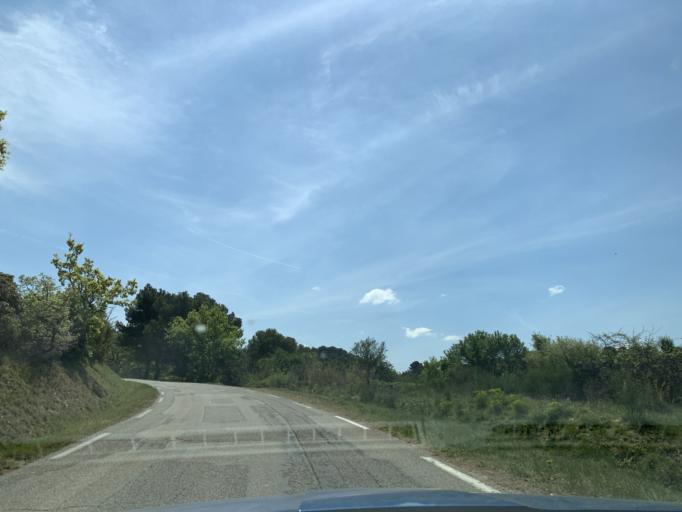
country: FR
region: Provence-Alpes-Cote d'Azur
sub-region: Departement du Vaucluse
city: Saint-Didier
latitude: 43.9942
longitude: 5.1058
